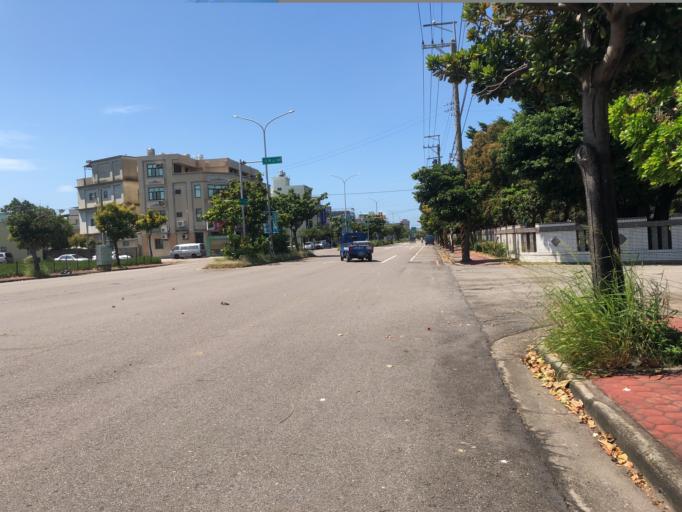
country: TW
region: Taiwan
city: Fengyuan
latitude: 24.2781
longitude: 120.5589
